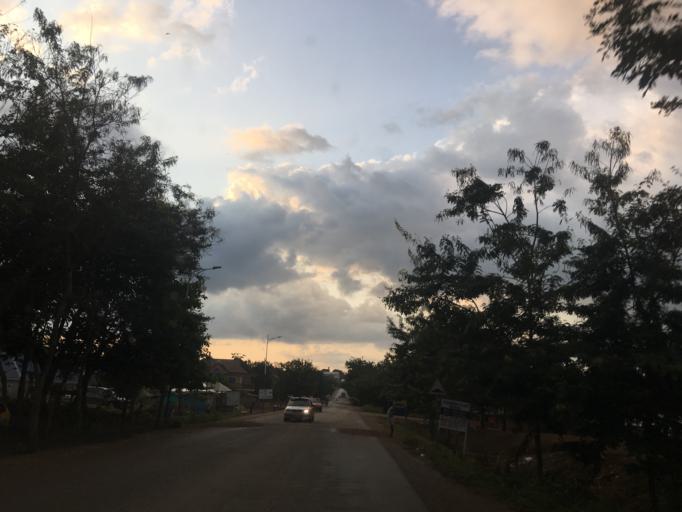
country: GH
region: Western
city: Bibiani
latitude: 6.7773
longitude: -2.5137
